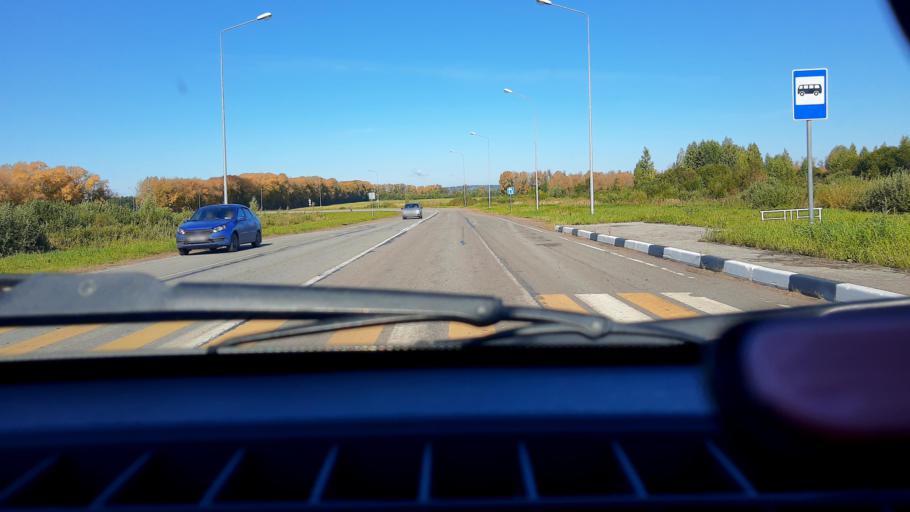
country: RU
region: Bashkortostan
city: Kushnarenkovo
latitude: 55.0633
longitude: 55.4266
